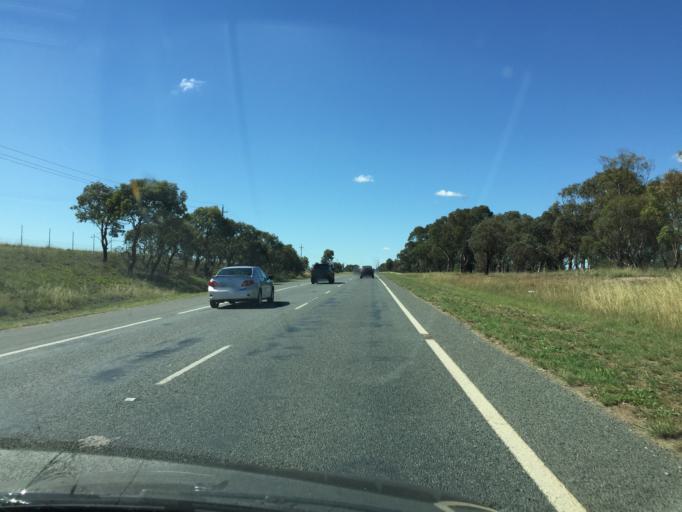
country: AU
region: Australian Capital Territory
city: Macarthur
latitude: -35.3783
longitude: 149.1695
